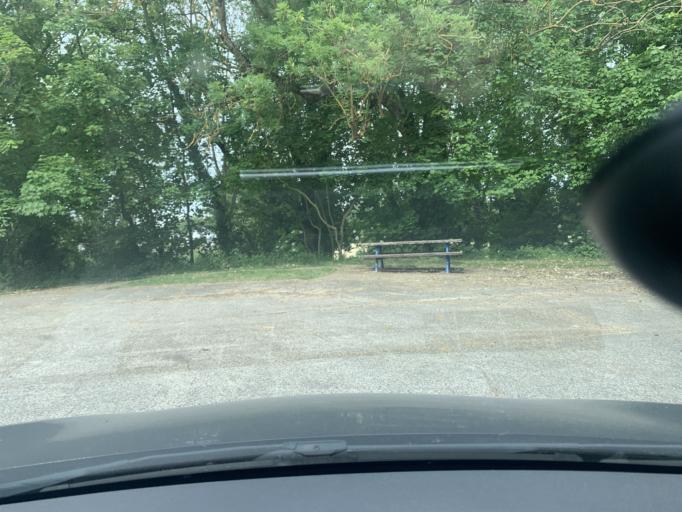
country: FR
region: Nord-Pas-de-Calais
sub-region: Departement du Nord
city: Marcoing
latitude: 50.1242
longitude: 3.1823
